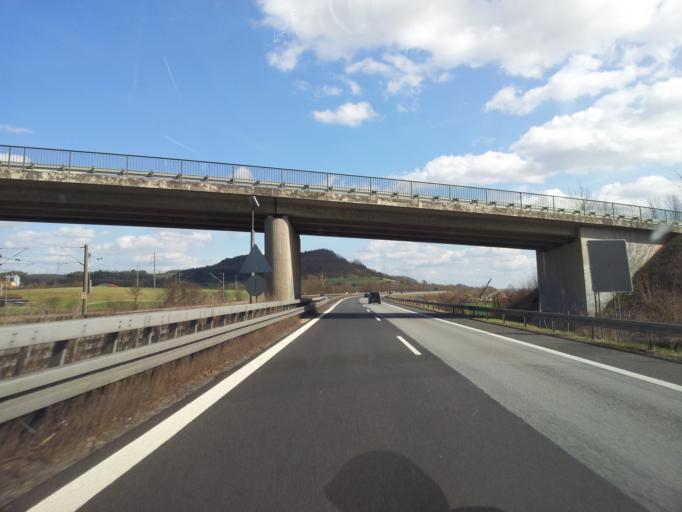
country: DE
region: Bavaria
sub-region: Regierungsbezirk Unterfranken
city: Stettfeld
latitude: 49.9662
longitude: 10.7206
